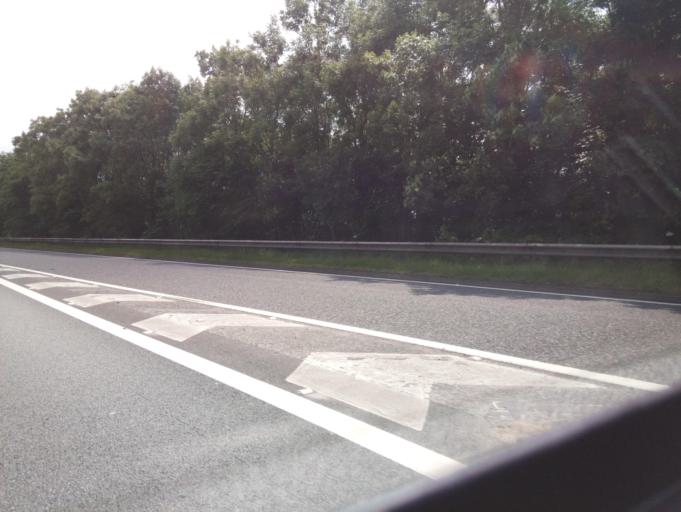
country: GB
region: England
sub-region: North Yorkshire
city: Thirsk
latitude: 54.2512
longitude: -1.3436
